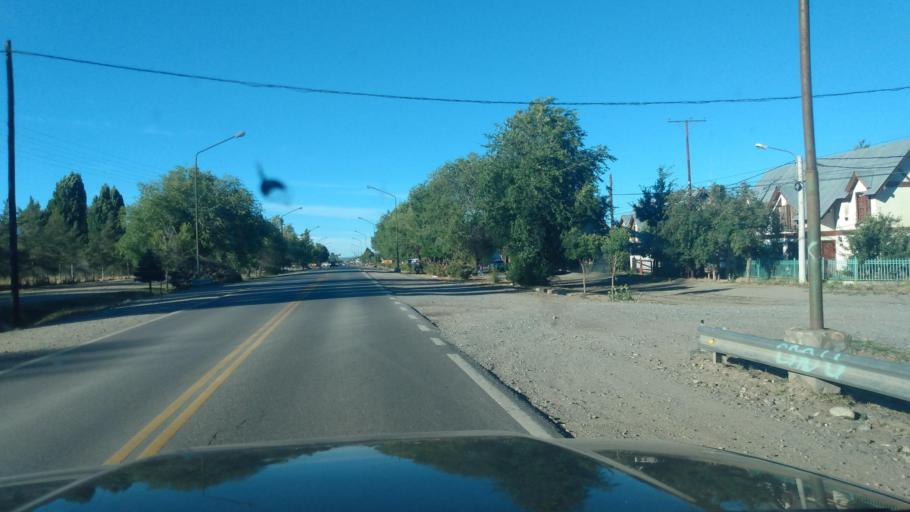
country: AR
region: Neuquen
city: Junin de los Andes
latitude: -39.9583
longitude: -71.0788
